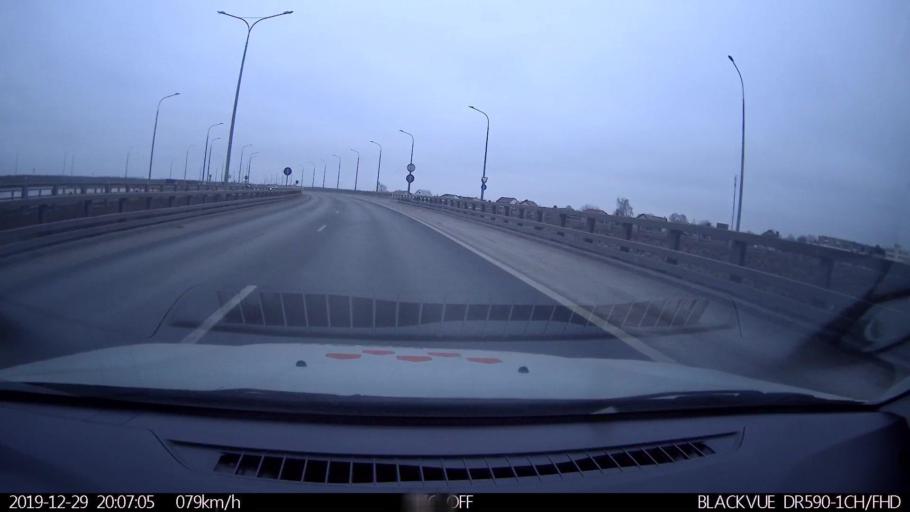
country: RU
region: Nizjnij Novgorod
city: Neklyudovo
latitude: 56.3967
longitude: 43.9885
